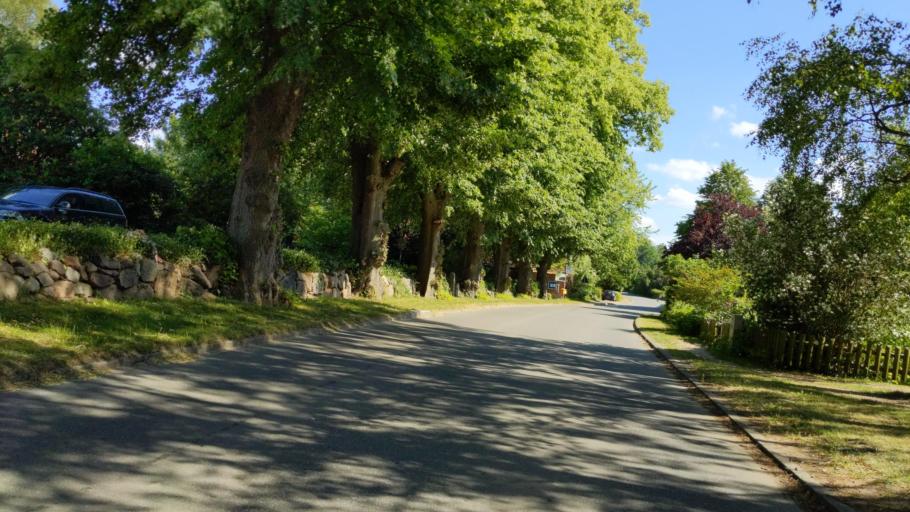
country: DE
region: Schleswig-Holstein
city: Goldenitz
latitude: 53.7148
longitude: 10.6470
